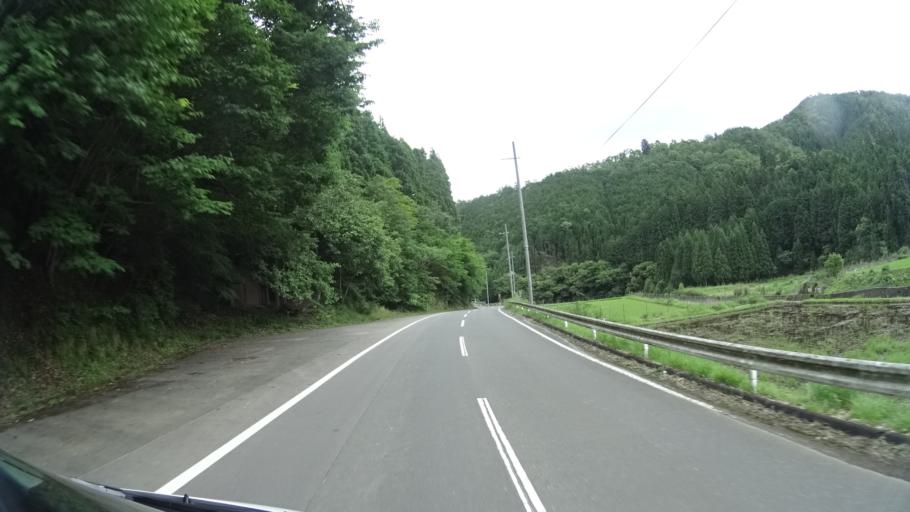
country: JP
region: Hyogo
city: Sasayama
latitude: 35.0590
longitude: 135.3921
